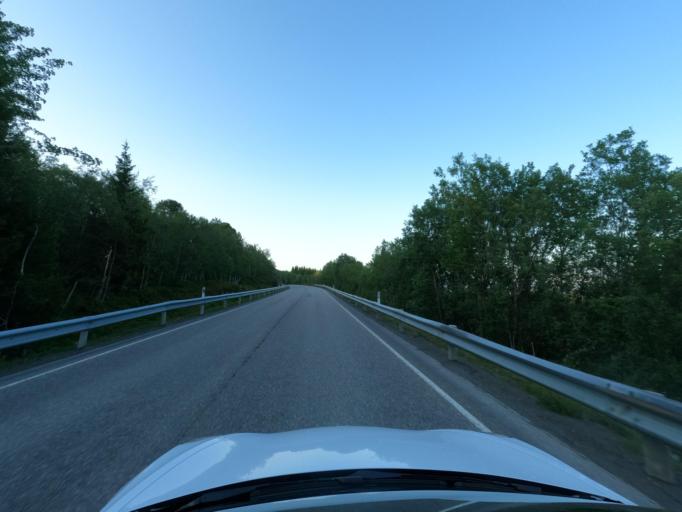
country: NO
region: Troms
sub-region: Harstad
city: Harstad
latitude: 68.7232
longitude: 16.5348
